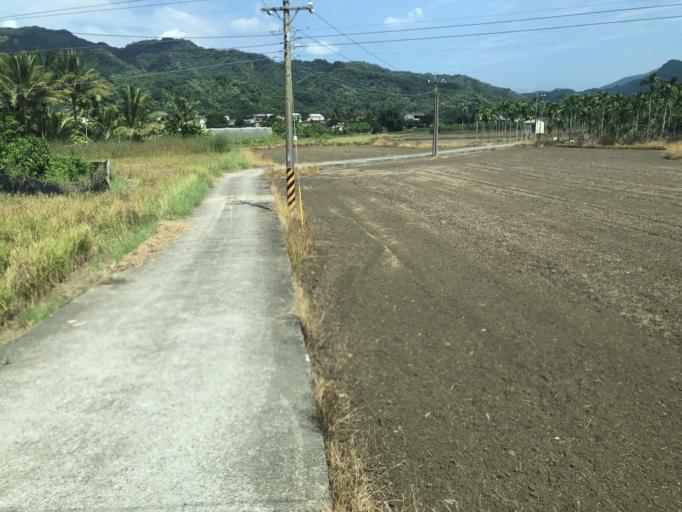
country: TW
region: Taiwan
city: Yujing
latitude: 22.9140
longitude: 120.5679
